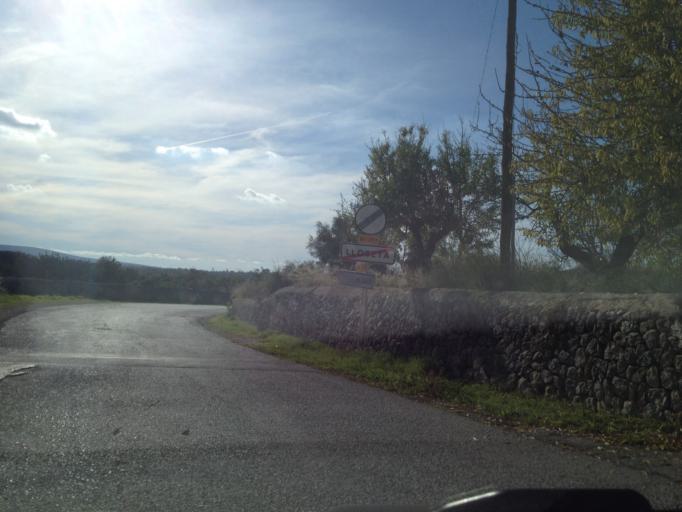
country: ES
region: Balearic Islands
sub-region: Illes Balears
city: Lloseta
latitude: 39.7161
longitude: 2.8593
